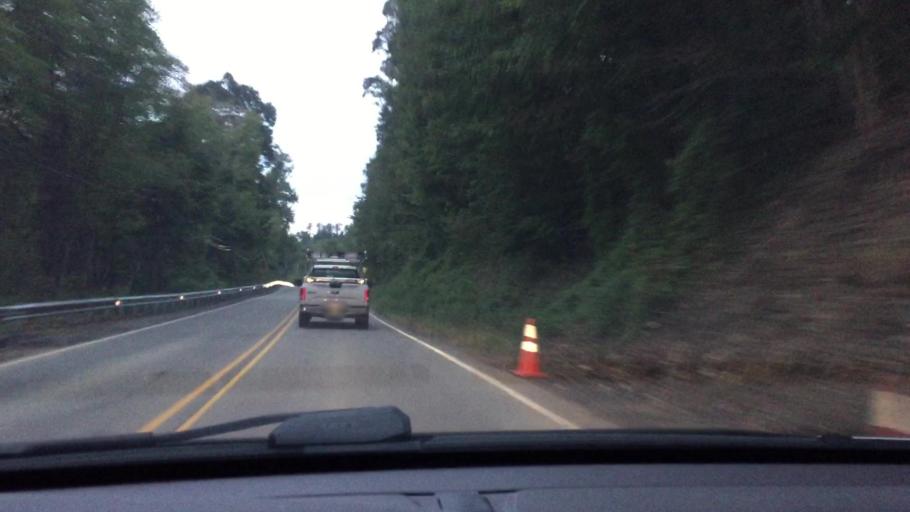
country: US
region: Pennsylvania
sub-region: Westmoreland County
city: West Newton
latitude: 40.2059
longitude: -79.7893
